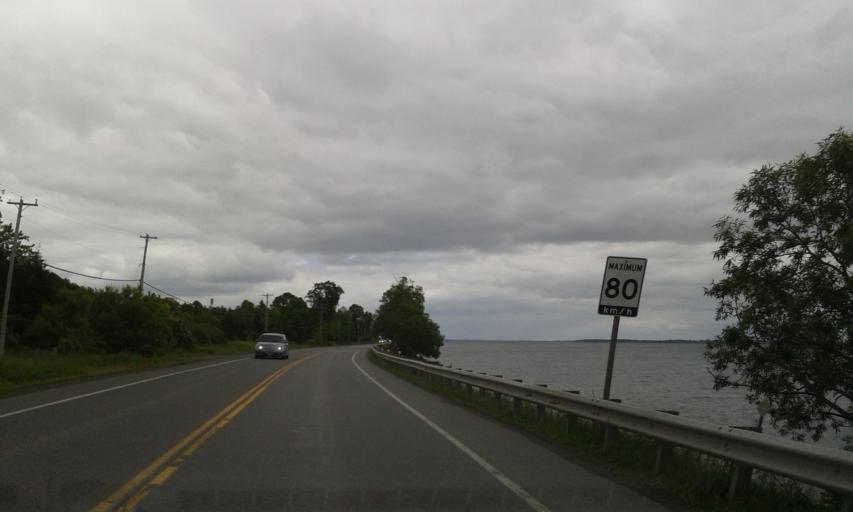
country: CA
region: Ontario
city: Skatepark
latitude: 44.1576
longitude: -76.8187
